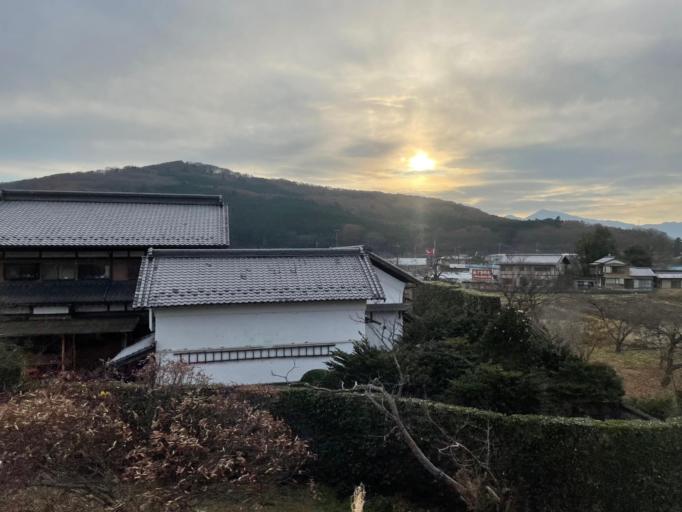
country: JP
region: Saitama
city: Ogawa
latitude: 36.0541
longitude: 139.2809
